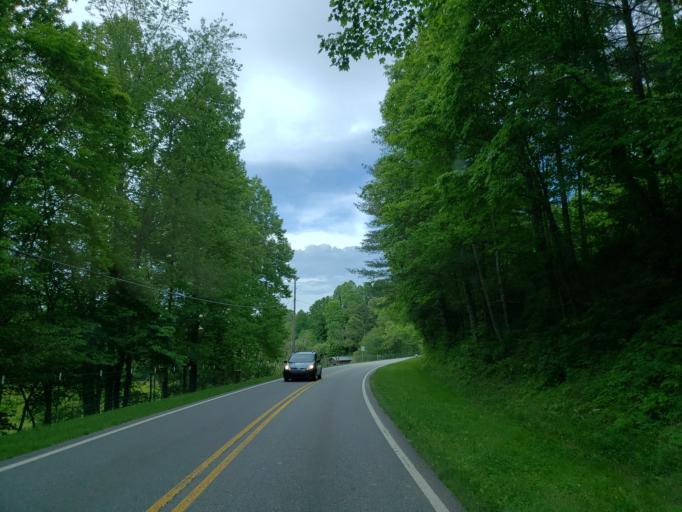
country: US
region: Georgia
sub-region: Fannin County
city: Blue Ridge
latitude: 34.8492
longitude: -84.3903
